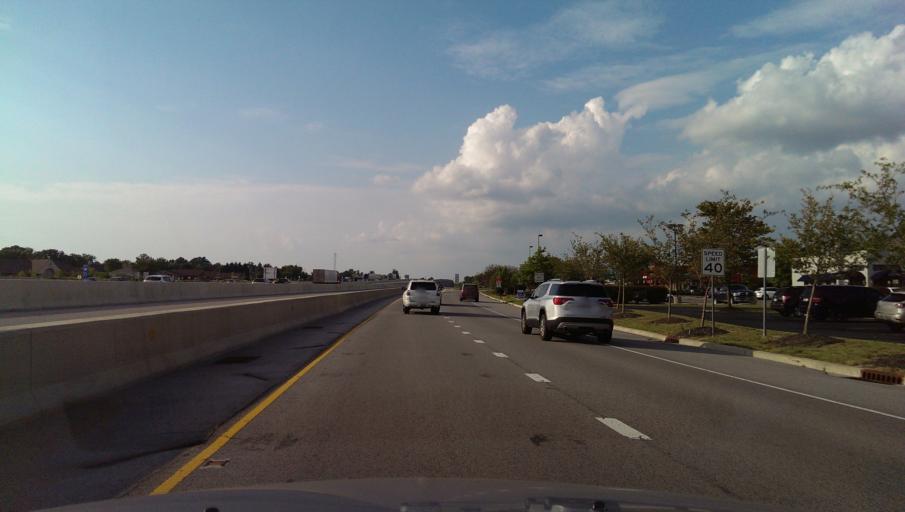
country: US
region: Indiana
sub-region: Hamilton County
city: Carmel
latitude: 40.0017
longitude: -86.1267
